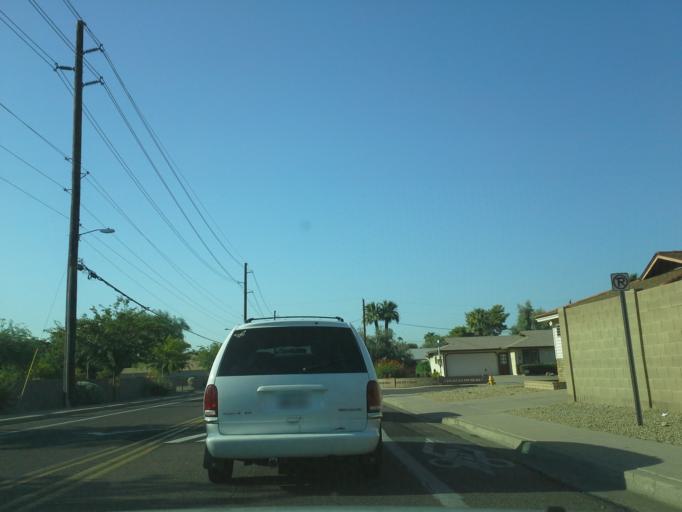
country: US
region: Arizona
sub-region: Maricopa County
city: Phoenix
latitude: 33.5375
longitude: -112.0912
